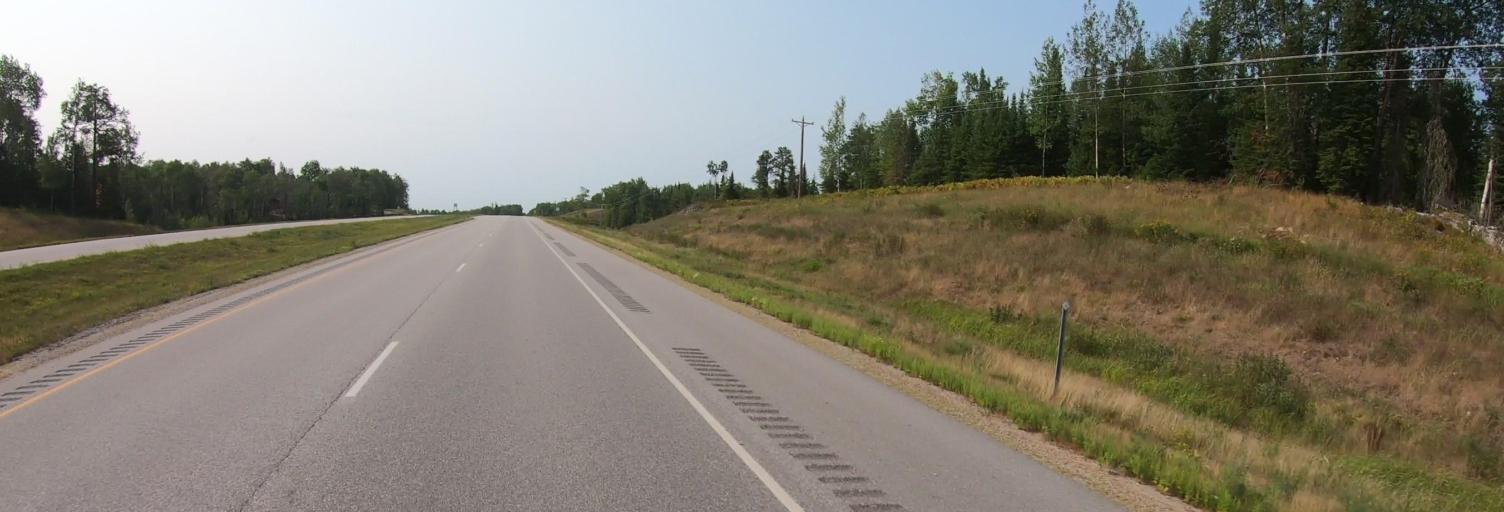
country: US
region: Minnesota
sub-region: Saint Louis County
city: Mountain Iron
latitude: 47.7617
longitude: -92.6543
